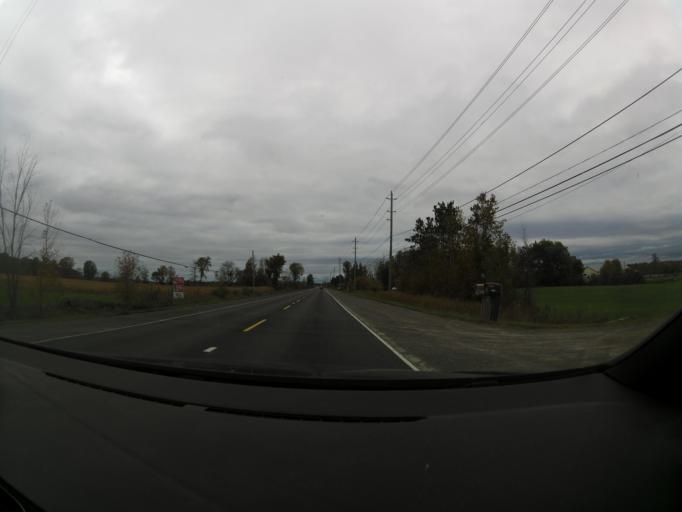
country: CA
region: Ontario
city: Bells Corners
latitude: 45.4372
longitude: -76.0409
